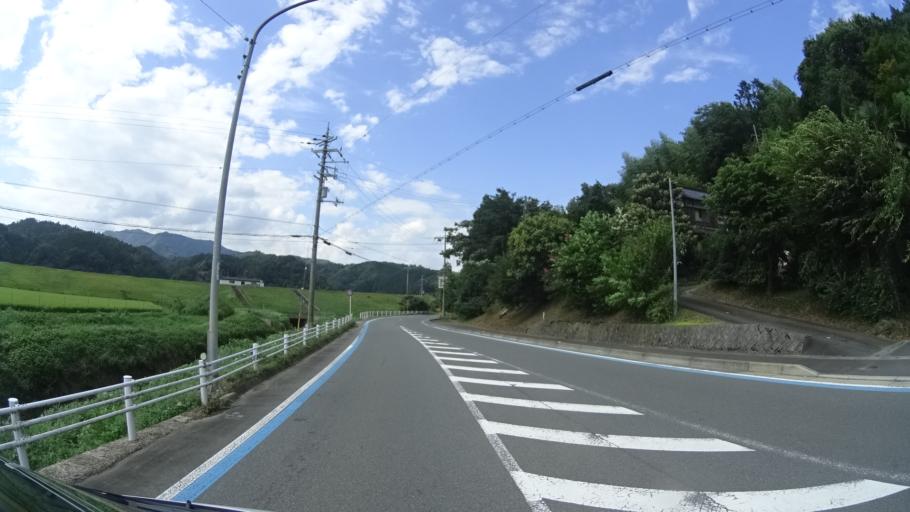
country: JP
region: Kyoto
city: Fukuchiyama
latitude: 35.3773
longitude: 135.1423
